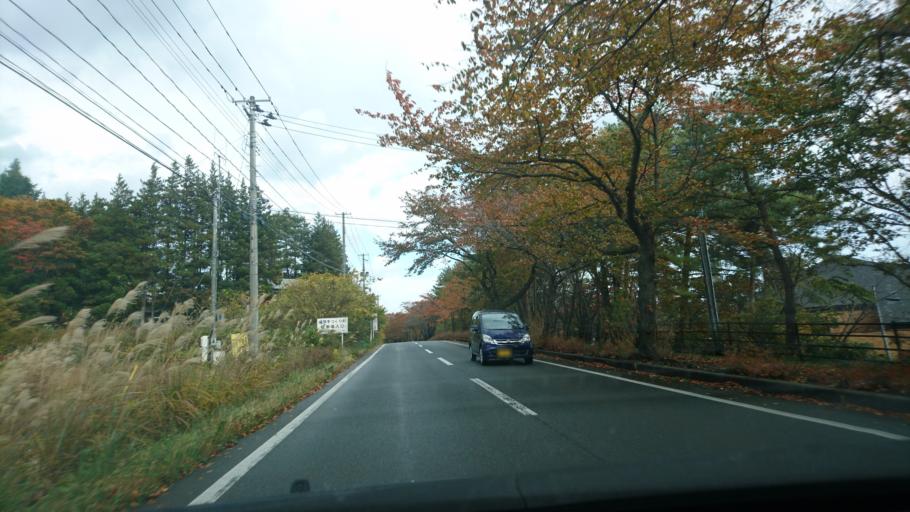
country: JP
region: Iwate
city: Shizukuishi
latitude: 39.6926
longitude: 141.0234
